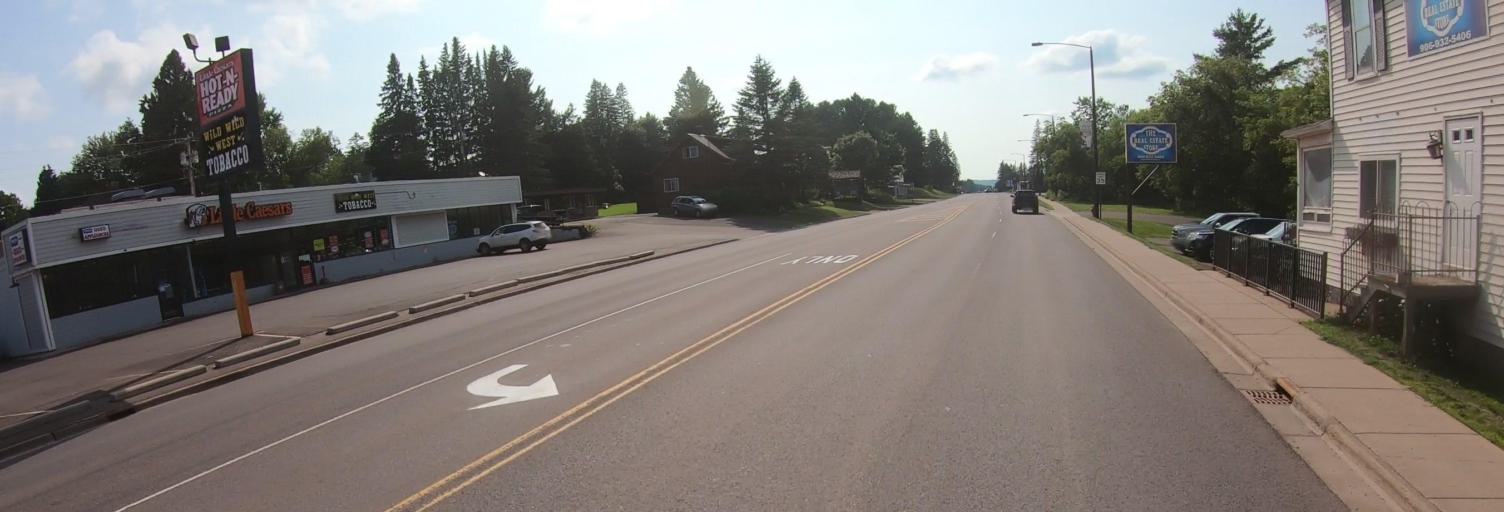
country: US
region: Michigan
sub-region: Gogebic County
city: Ironwood
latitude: 46.4634
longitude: -90.1565
